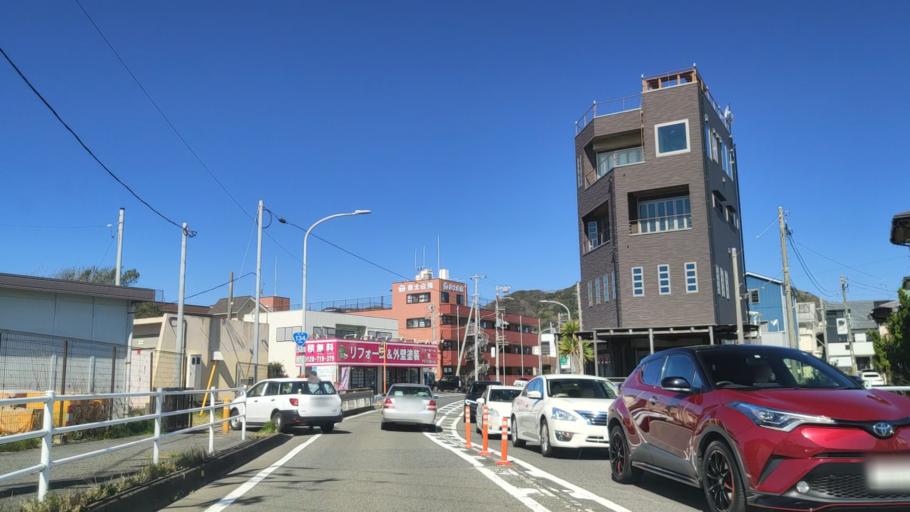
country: JP
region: Kanagawa
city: Hiratsuka
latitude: 35.3141
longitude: 139.3308
